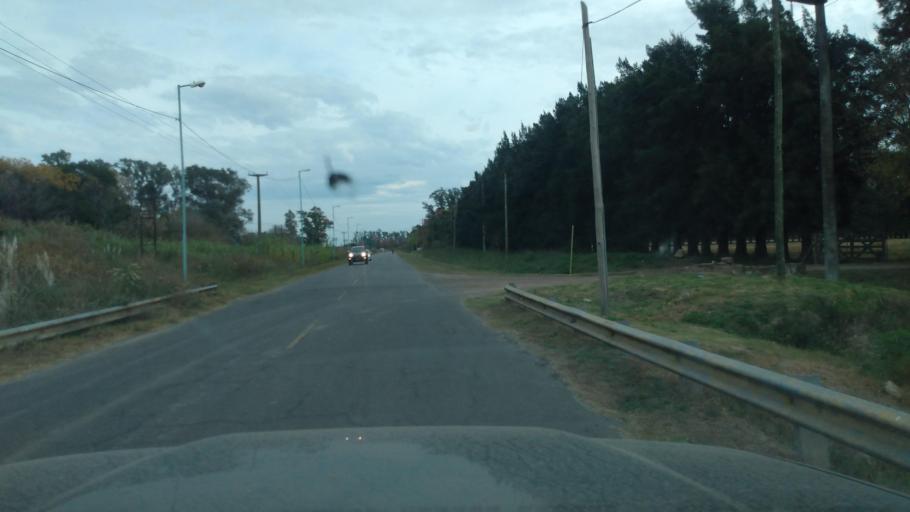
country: AR
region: Buenos Aires
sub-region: Partido de Lujan
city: Lujan
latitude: -34.5946
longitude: -59.1544
